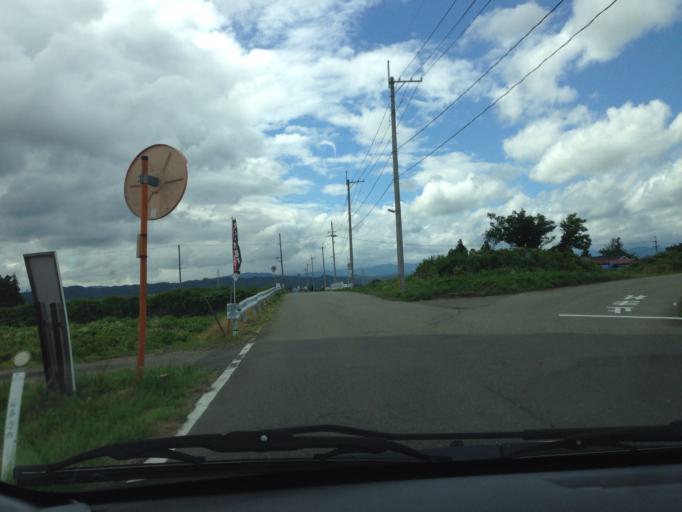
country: JP
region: Fukushima
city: Kitakata
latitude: 37.6380
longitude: 139.9001
